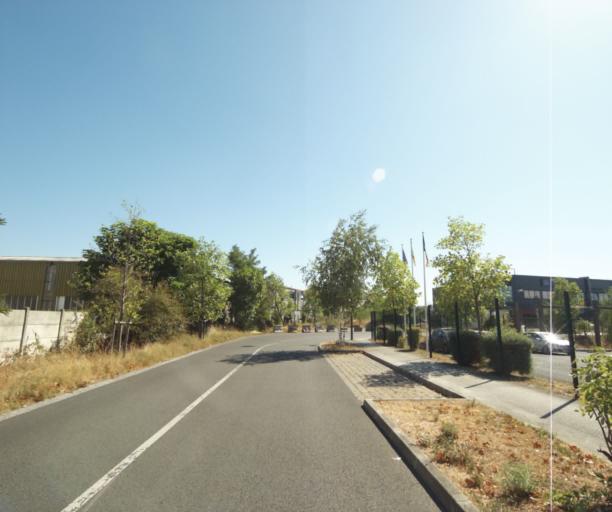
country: FR
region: Ile-de-France
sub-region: Departement des Hauts-de-Seine
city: Villeneuve-la-Garenne
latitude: 48.9278
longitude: 2.3233
